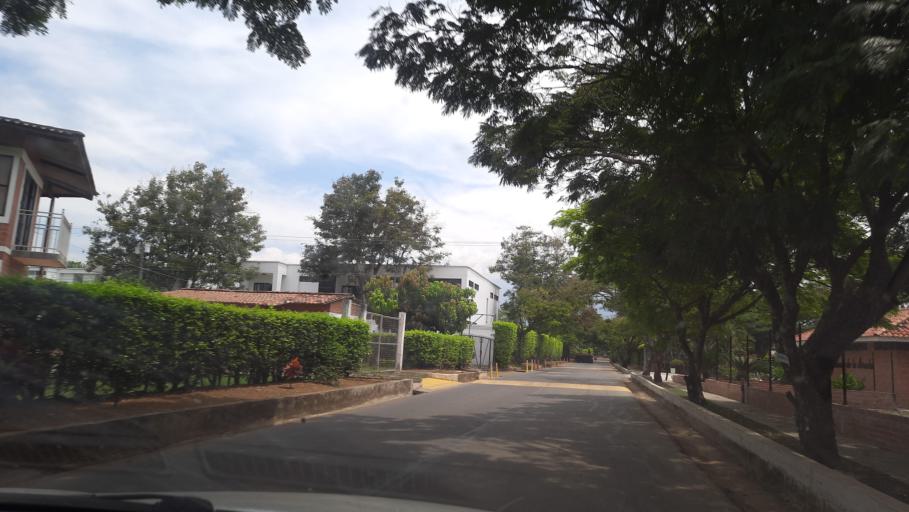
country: CO
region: Valle del Cauca
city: Jamundi
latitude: 3.2697
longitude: -76.5193
